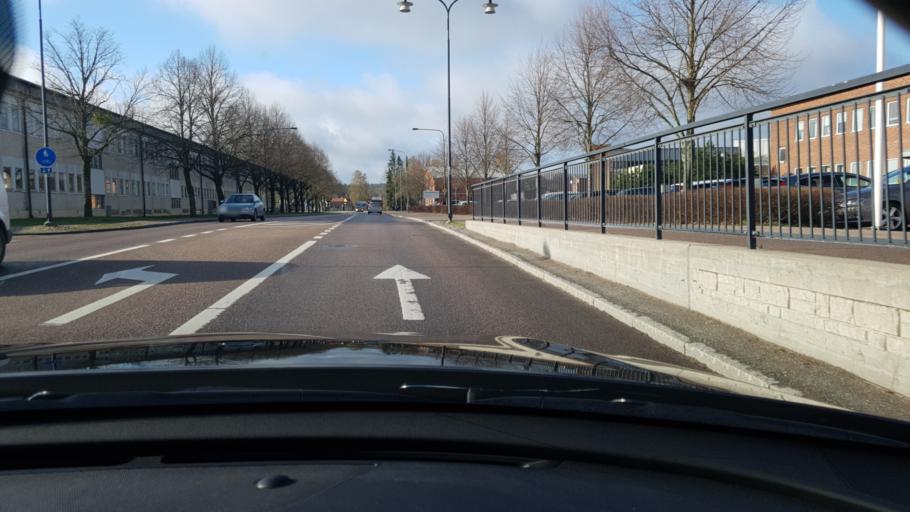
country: SE
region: Vaestmanland
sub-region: Arboga Kommun
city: Arboga
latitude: 59.3965
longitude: 15.8332
